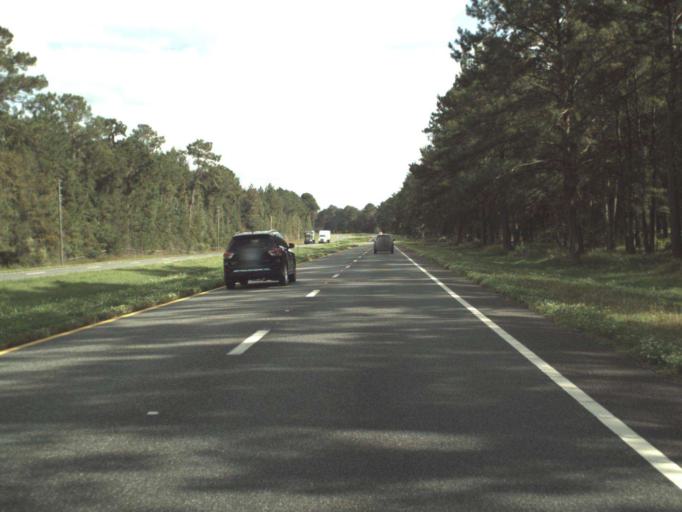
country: US
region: Florida
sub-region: Jefferson County
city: Monticello
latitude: 30.3939
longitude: -83.8699
